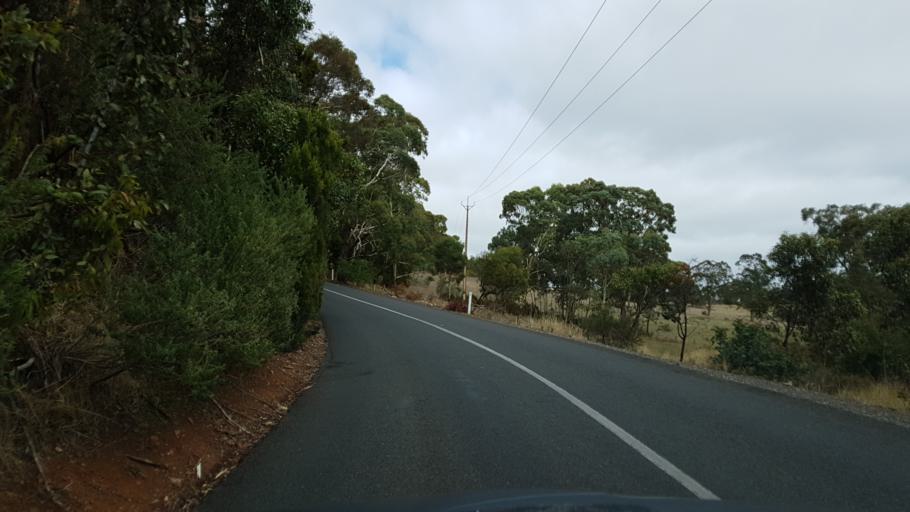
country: AU
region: South Australia
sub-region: Mount Barker
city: Little Hampton
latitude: -35.0793
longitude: 138.8265
